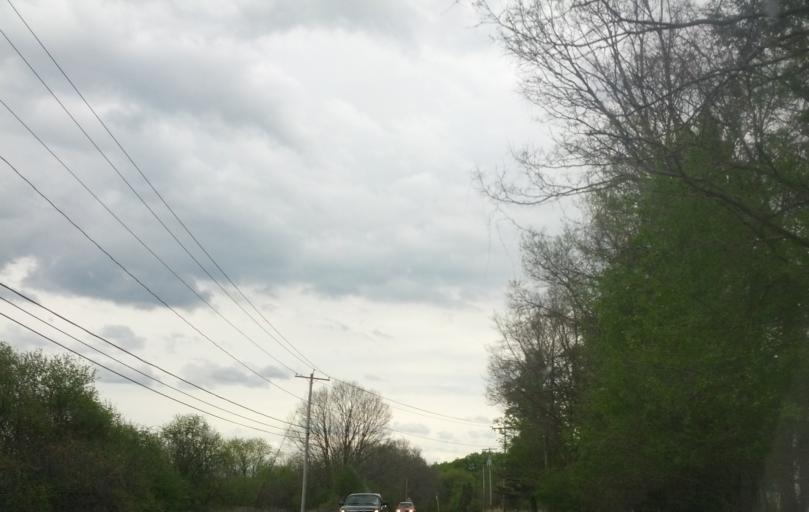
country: US
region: New York
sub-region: Onondaga County
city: Fayetteville
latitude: 42.9912
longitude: -76.0169
